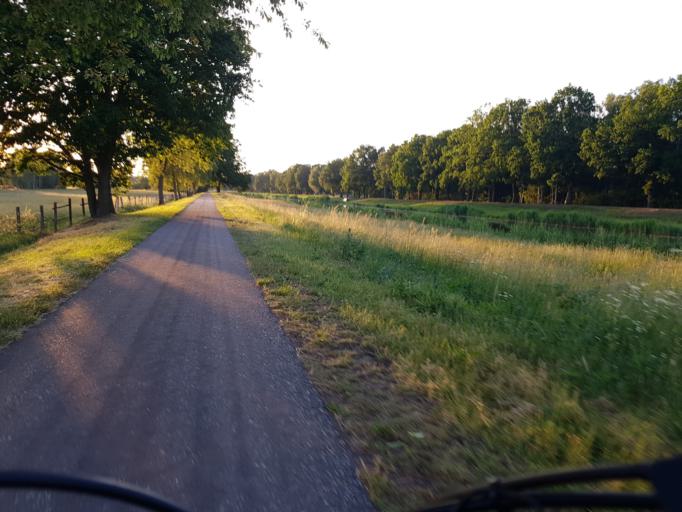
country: DE
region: Brandenburg
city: Schilda
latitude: 51.5774
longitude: 13.3454
